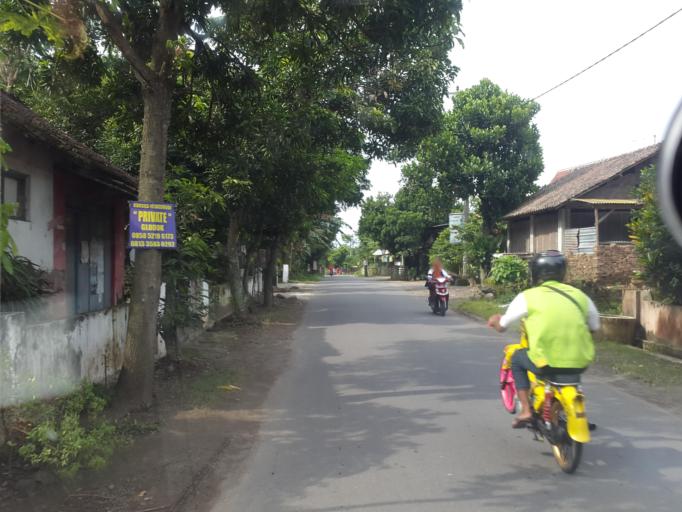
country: ID
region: East Java
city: Madiun
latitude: -7.5720
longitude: 111.3771
